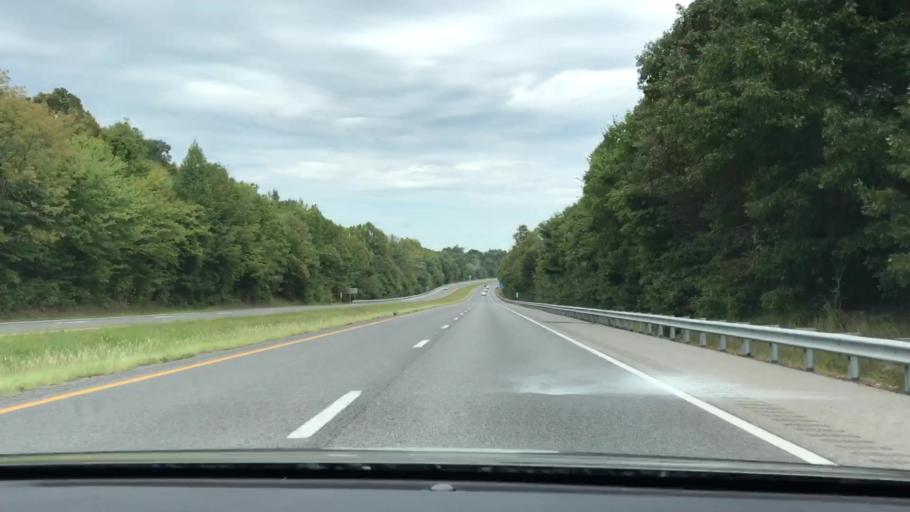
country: US
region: Kentucky
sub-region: Marshall County
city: Benton
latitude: 36.9139
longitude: -88.3501
